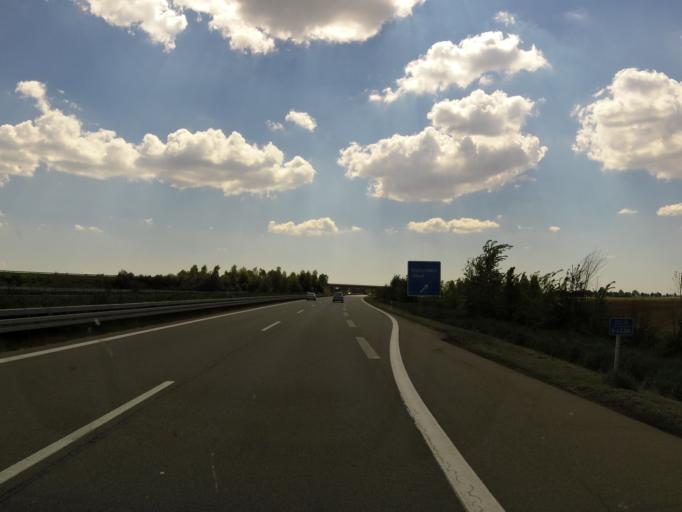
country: DE
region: Bavaria
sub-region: Lower Bavaria
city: Wallersdorf
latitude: 48.7303
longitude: 12.7300
